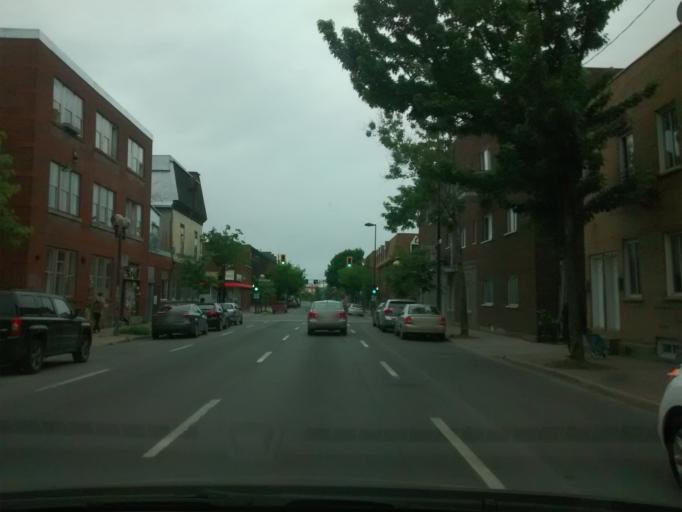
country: CA
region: Quebec
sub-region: Monteregie
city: Longueuil
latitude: 45.5298
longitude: -73.5469
